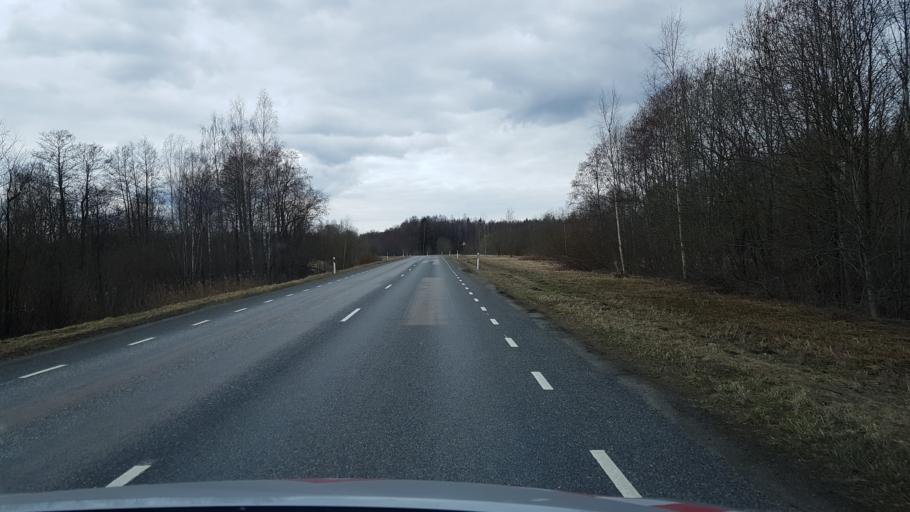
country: EE
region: Ida-Virumaa
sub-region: Narva-Joesuu linn
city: Narva-Joesuu
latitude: 59.3511
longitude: 28.0469
